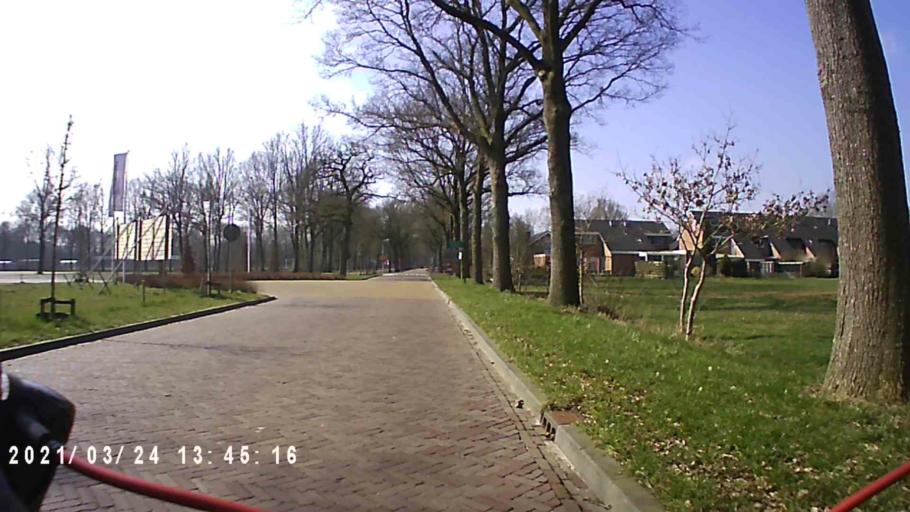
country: NL
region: Groningen
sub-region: Gemeente Grootegast
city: Grootegast
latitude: 53.0829
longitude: 6.2640
